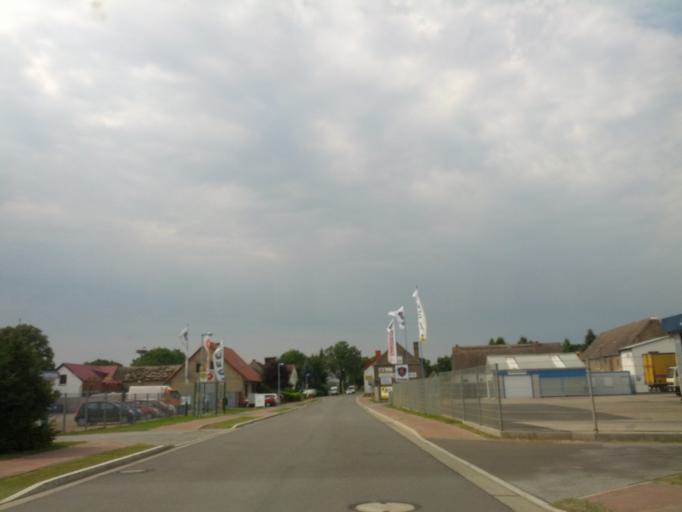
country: DE
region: Brandenburg
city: Fehrbellin
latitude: 52.7774
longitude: 12.8339
